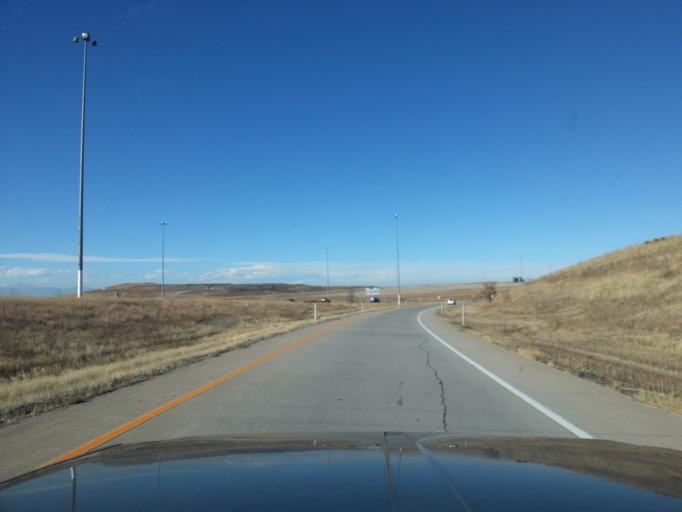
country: US
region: Colorado
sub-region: Adams County
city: Aurora
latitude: 39.8380
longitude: -104.7456
